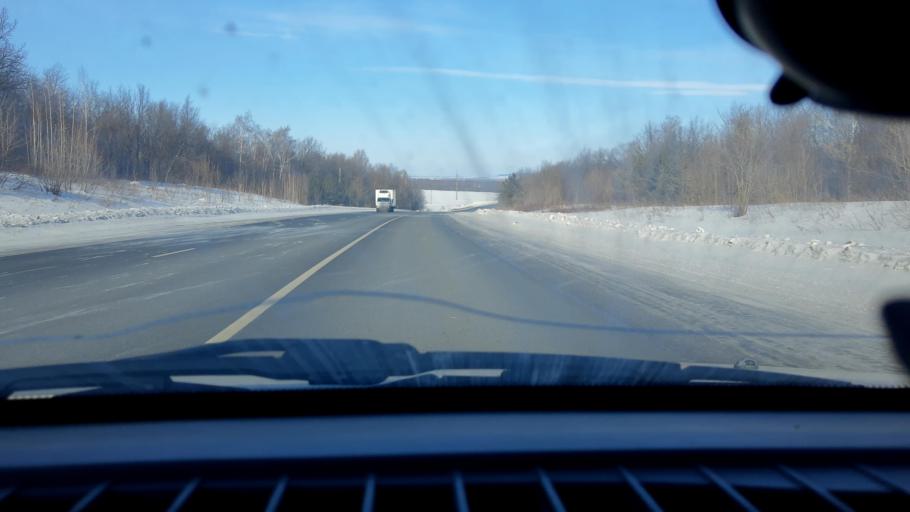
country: RU
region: Bashkortostan
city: Avdon
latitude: 54.8469
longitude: 55.7077
